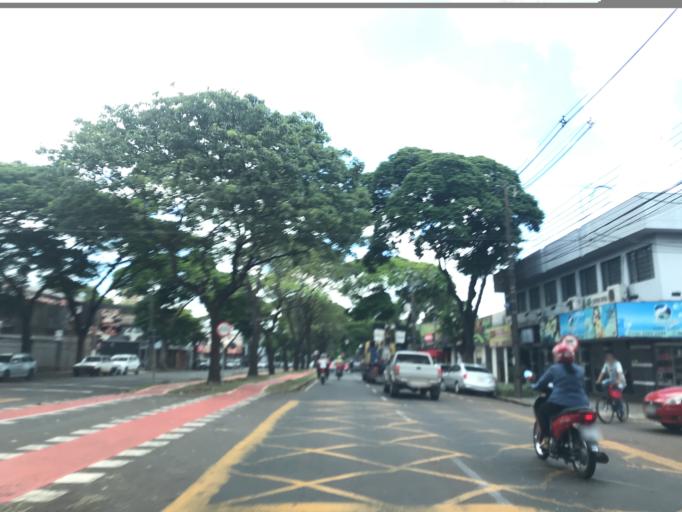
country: BR
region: Parana
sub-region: Maringa
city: Maringa
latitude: -23.4120
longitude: -51.9249
